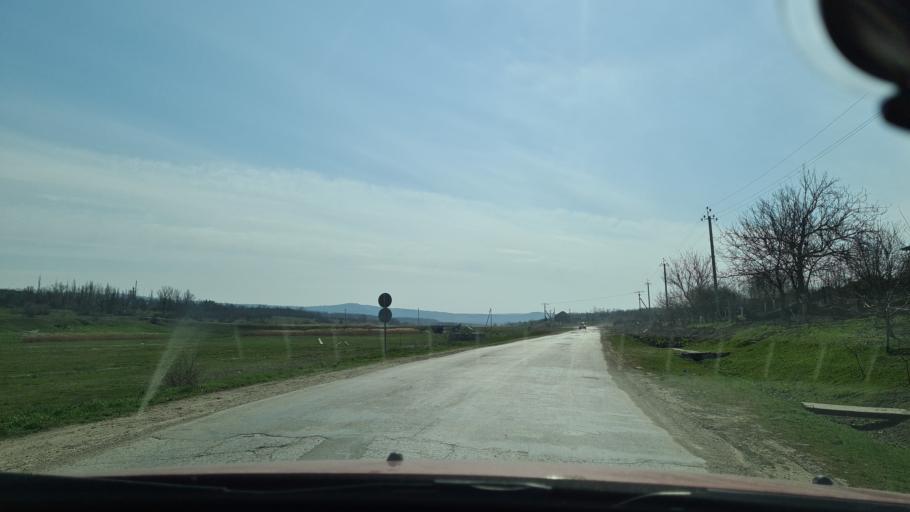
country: MD
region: Ungheni
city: Ungheni
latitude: 47.3197
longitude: 27.8973
